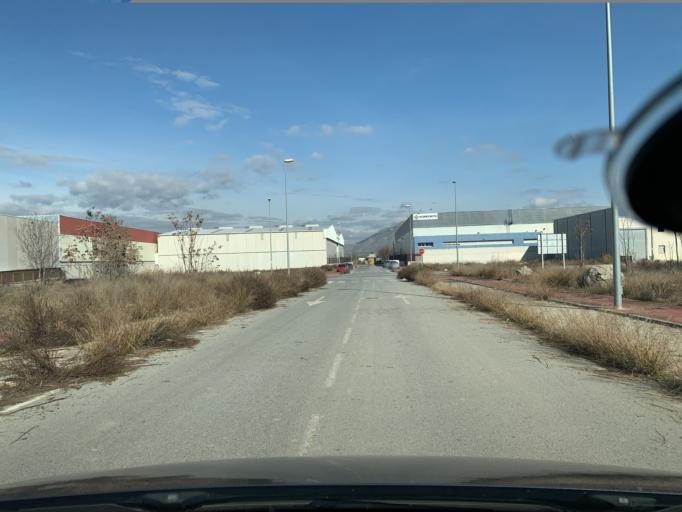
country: ES
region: Andalusia
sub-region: Provincia de Granada
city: Chauchina
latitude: 37.1885
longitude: -3.7487
